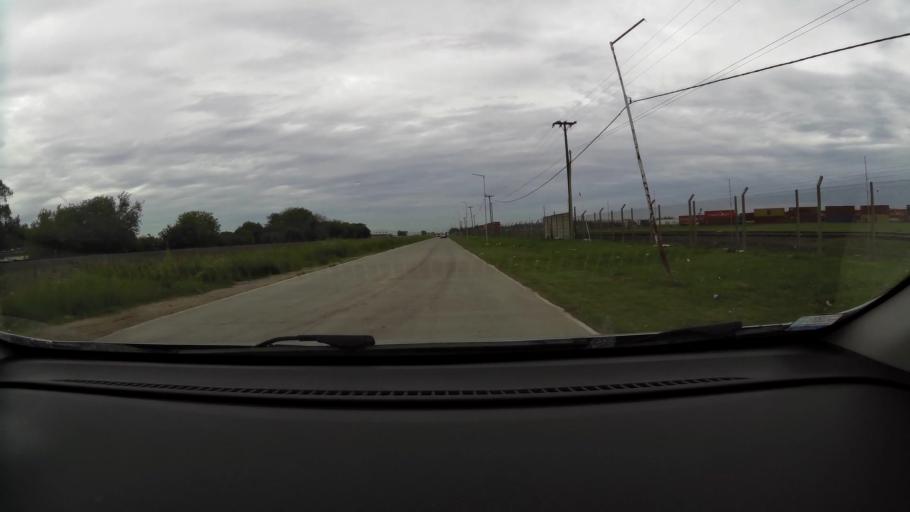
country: AR
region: Buenos Aires
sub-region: Partido de Zarate
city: Zarate
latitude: -34.0891
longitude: -59.0582
